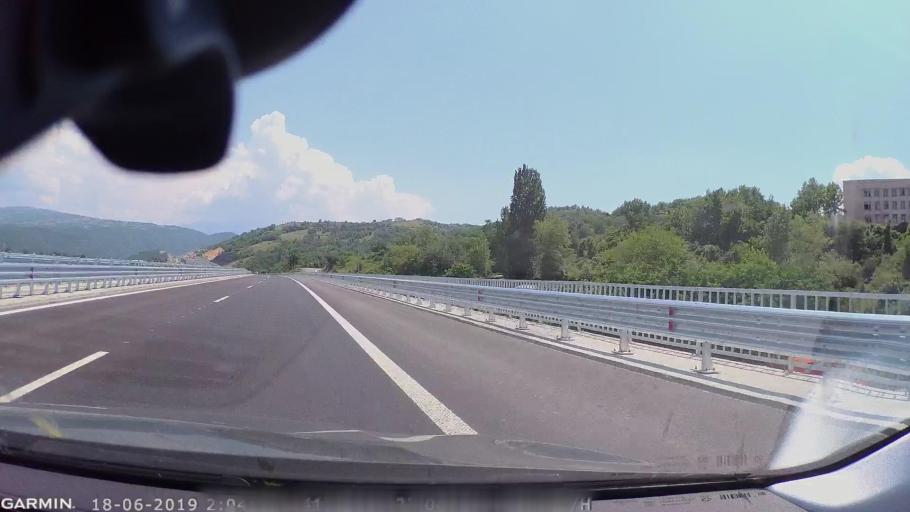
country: BG
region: Blagoevgrad
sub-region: Obshtina Blagoevgrad
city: Blagoevgrad
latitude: 41.9812
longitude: 23.0621
